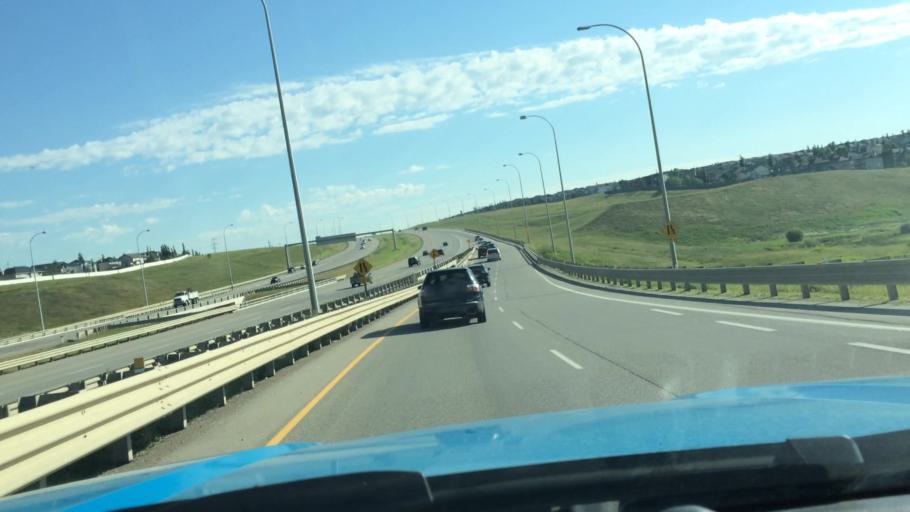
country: CA
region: Alberta
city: Calgary
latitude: 51.1575
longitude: -114.1137
